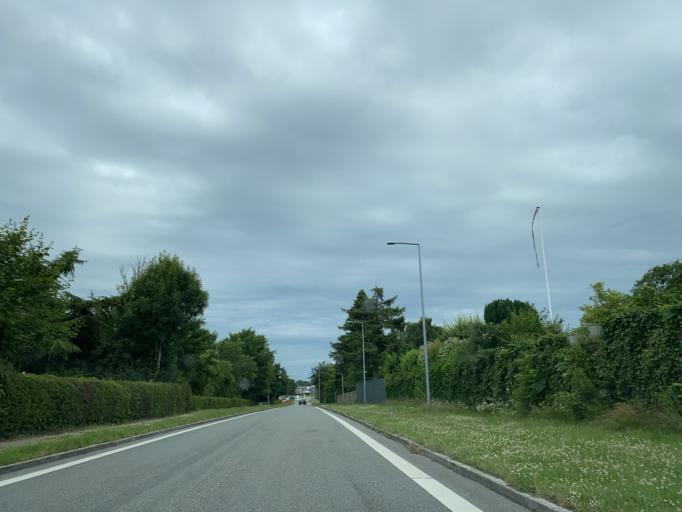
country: DK
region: South Denmark
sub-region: Sonderborg Kommune
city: Sonderborg
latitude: 54.9212
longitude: 9.7988
